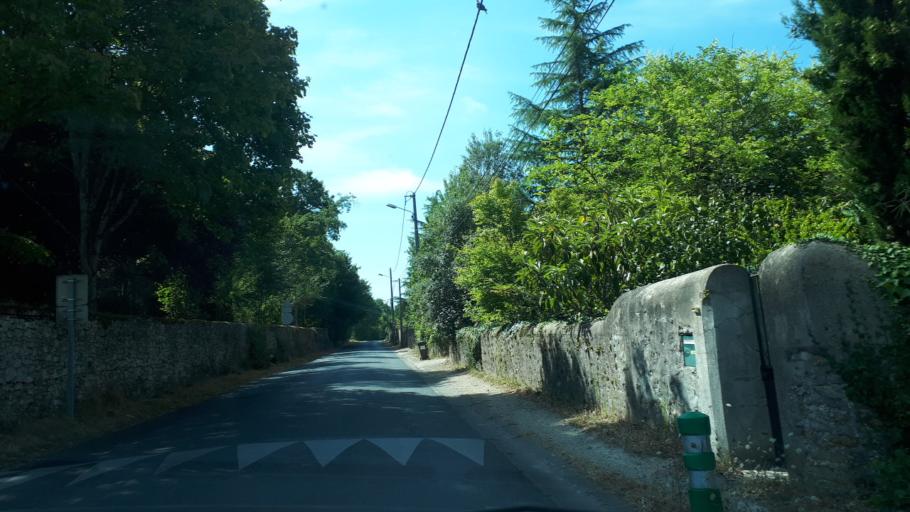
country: FR
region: Centre
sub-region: Departement du Loir-et-Cher
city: Cellettes
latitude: 47.5227
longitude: 1.3858
